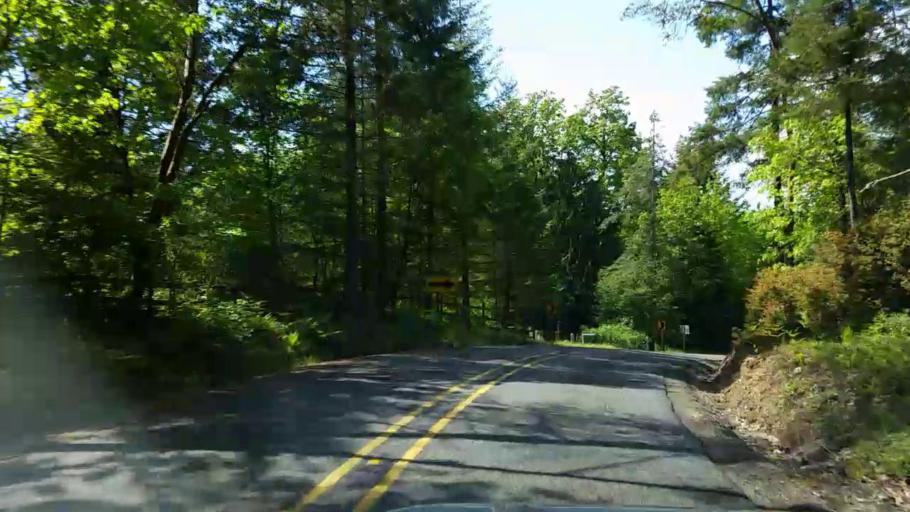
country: US
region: Washington
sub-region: Pierce County
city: Key Center
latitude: 47.3388
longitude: -122.7582
